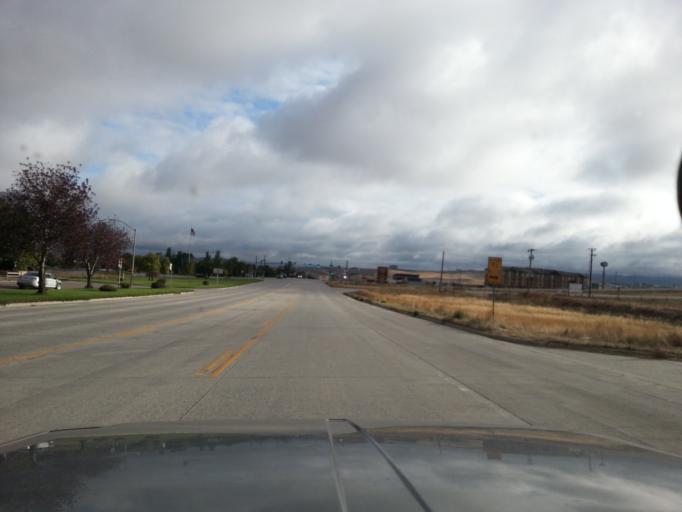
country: US
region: Wyoming
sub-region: Converse County
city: Douglas
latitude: 42.7641
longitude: -105.4069
